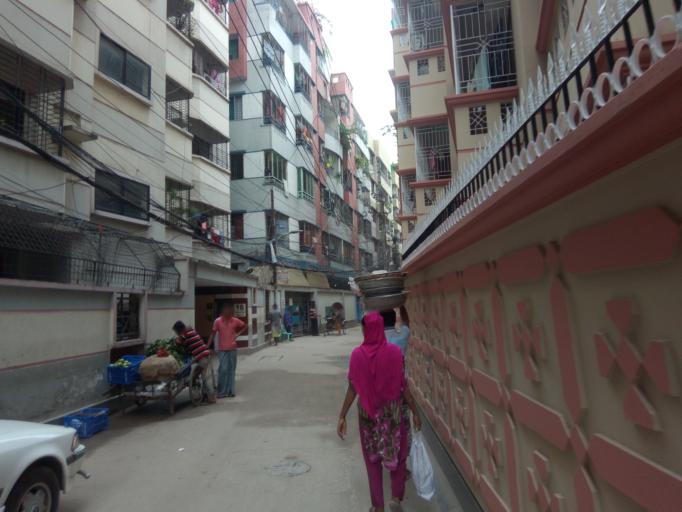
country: BD
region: Dhaka
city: Paltan
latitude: 23.7453
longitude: 90.4098
